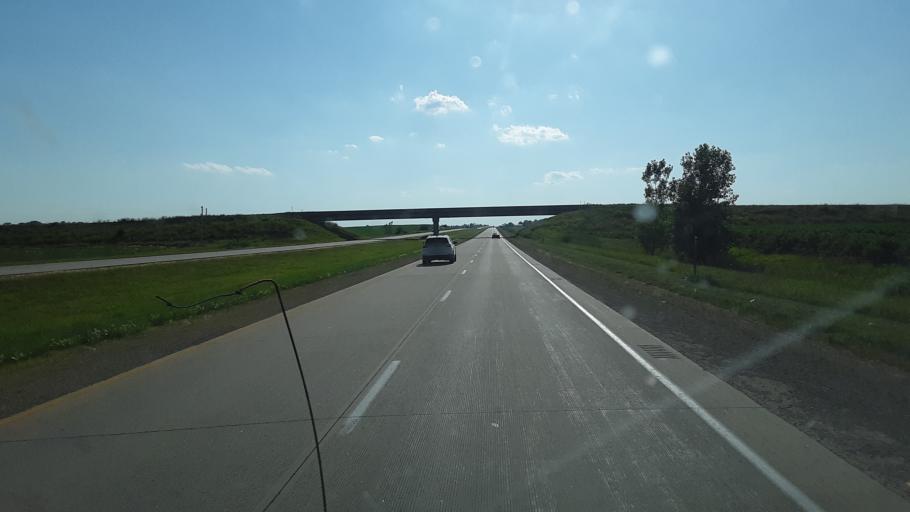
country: US
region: Iowa
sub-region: Grundy County
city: Dike
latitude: 42.4636
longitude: -92.7076
